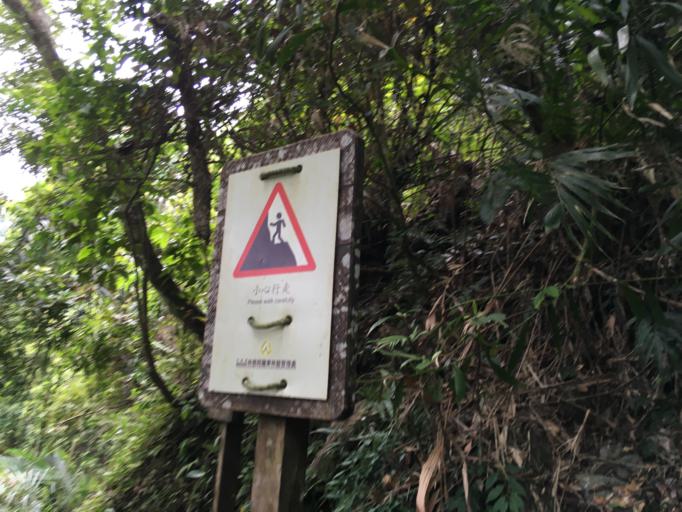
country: TW
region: Taiwan
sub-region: Yilan
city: Yilan
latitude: 24.4246
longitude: 121.7024
